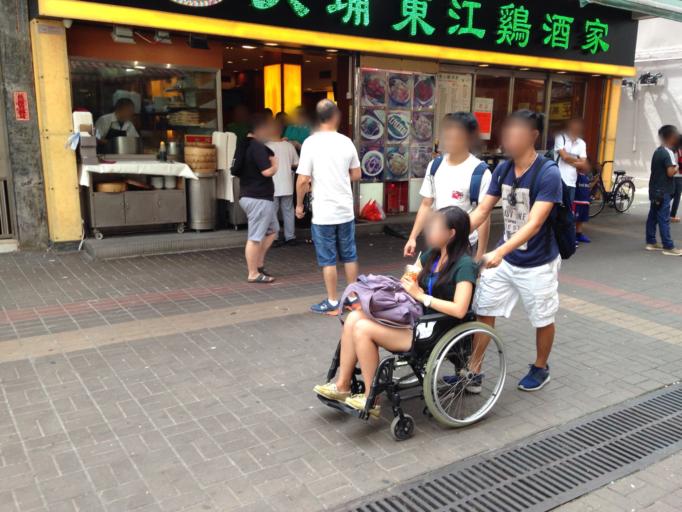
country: HK
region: Tai Po
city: Tai Po
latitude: 22.4474
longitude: 114.1679
